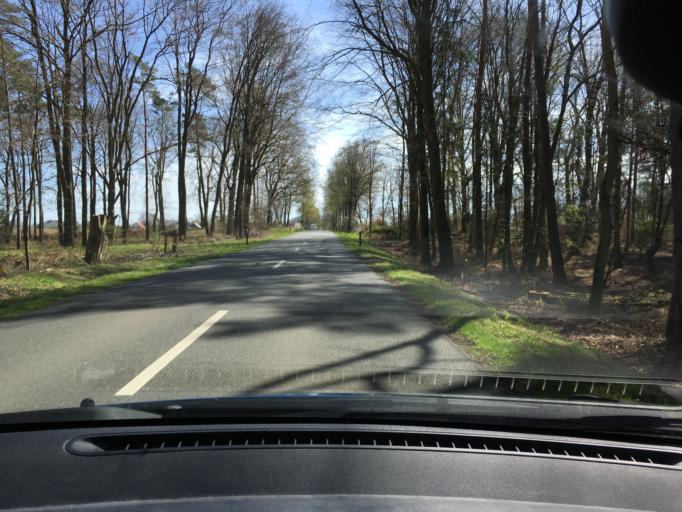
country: DE
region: Lower Saxony
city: Romstedt
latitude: 53.1339
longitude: 10.6897
